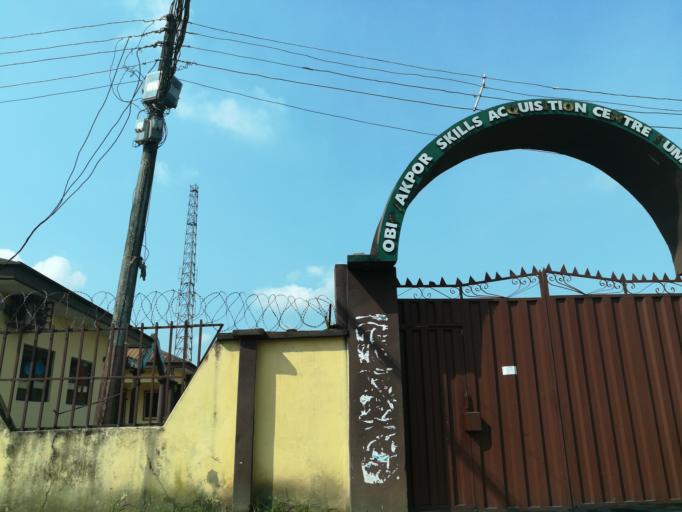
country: NG
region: Rivers
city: Port Harcourt
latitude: 4.8318
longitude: 6.9843
